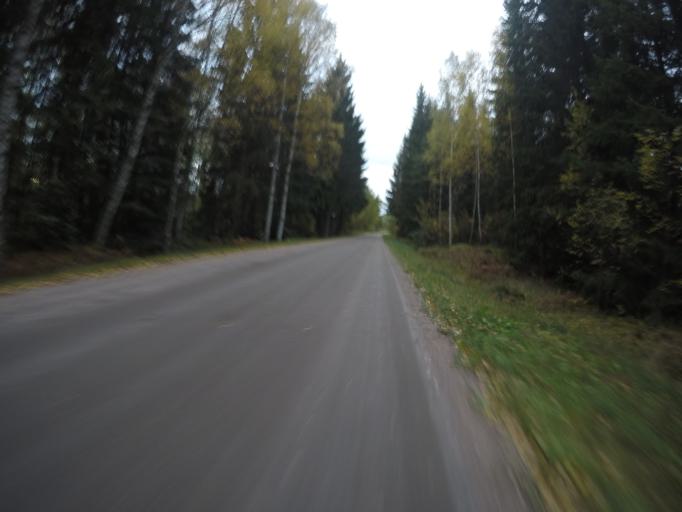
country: SE
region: Vaestmanland
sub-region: Arboga Kommun
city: Tyringe
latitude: 59.3333
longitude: 15.9673
